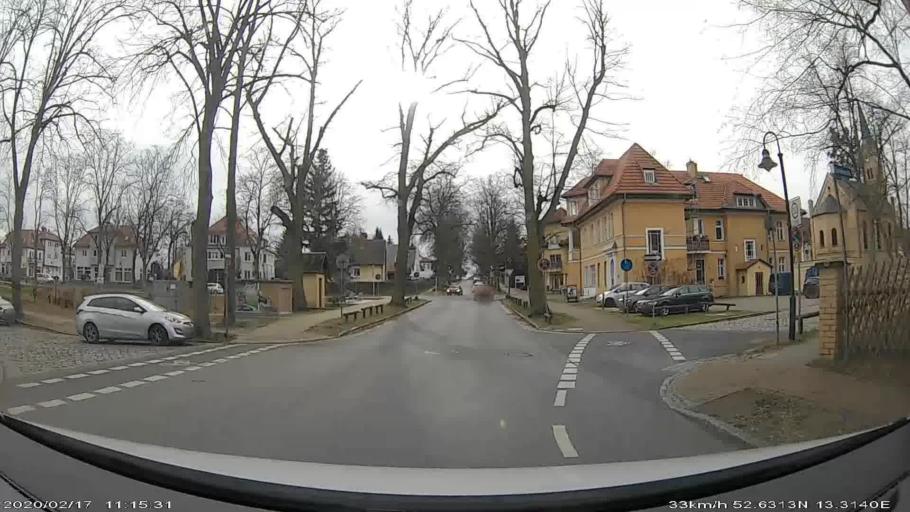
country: DE
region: Brandenburg
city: Glienicke
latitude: 52.6313
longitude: 13.3140
